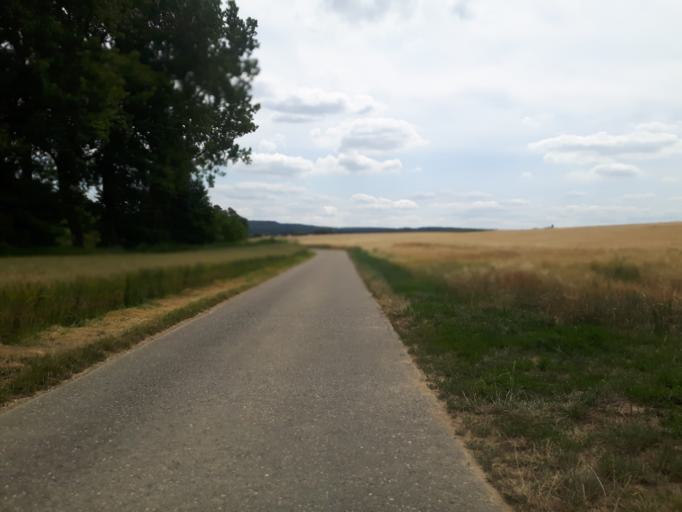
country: DE
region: Baden-Wuerttemberg
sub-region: Regierungsbezirk Stuttgart
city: Eppingen
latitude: 49.1228
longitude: 8.8895
